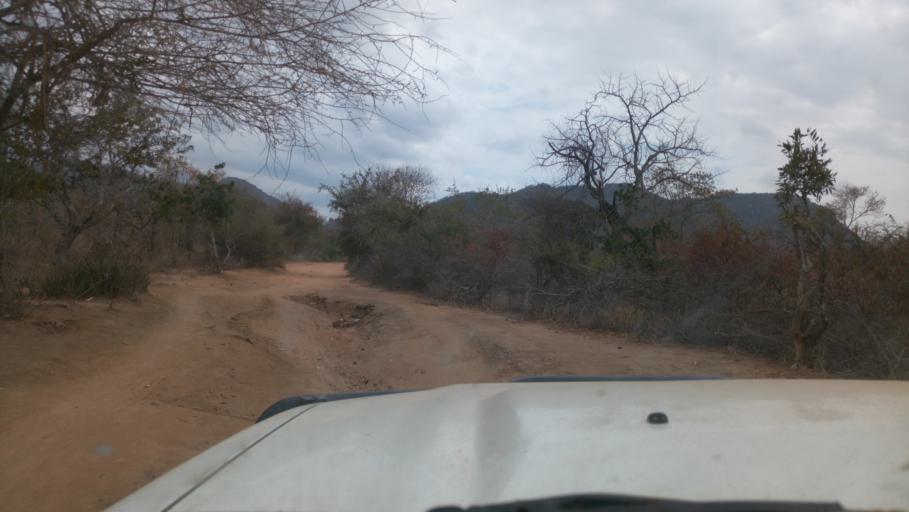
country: KE
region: Kitui
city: Kitui
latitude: -1.8164
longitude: 38.4274
